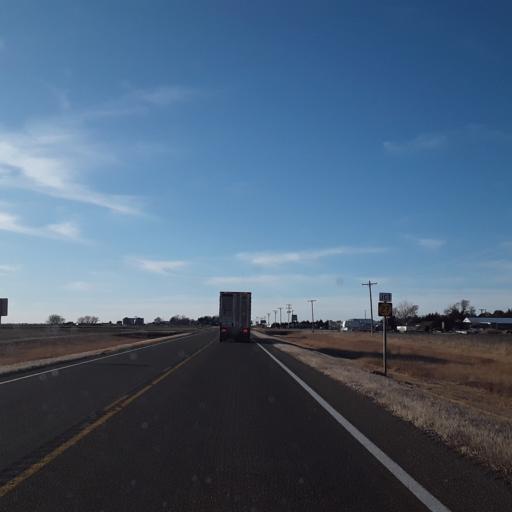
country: US
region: Kansas
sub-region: Cheyenne County
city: Saint Francis
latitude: 39.7566
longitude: -101.7073
